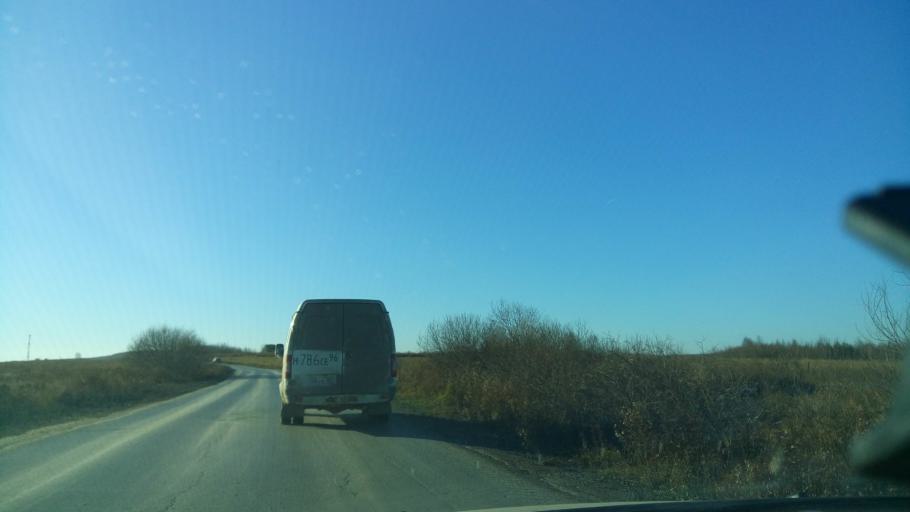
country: RU
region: Sverdlovsk
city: Sovkhoznyy
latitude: 56.7300
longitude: 60.5364
